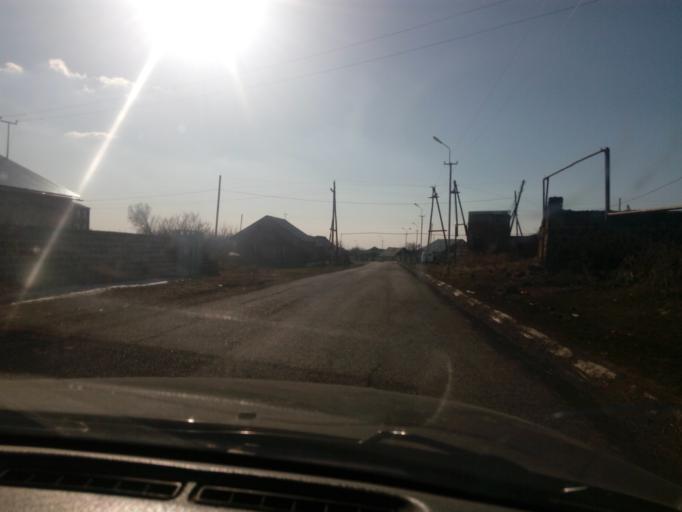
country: AM
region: Kotayk'i Marz
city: Zarr
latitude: 40.2597
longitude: 44.7525
